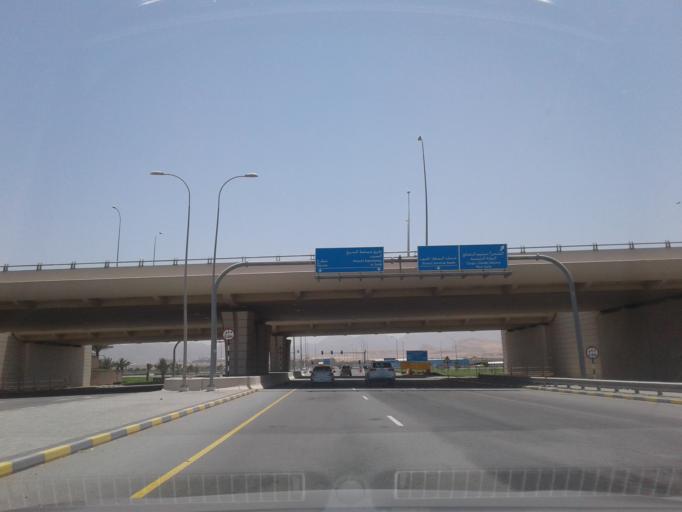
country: OM
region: Muhafazat Masqat
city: Bawshar
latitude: 23.6037
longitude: 58.3115
